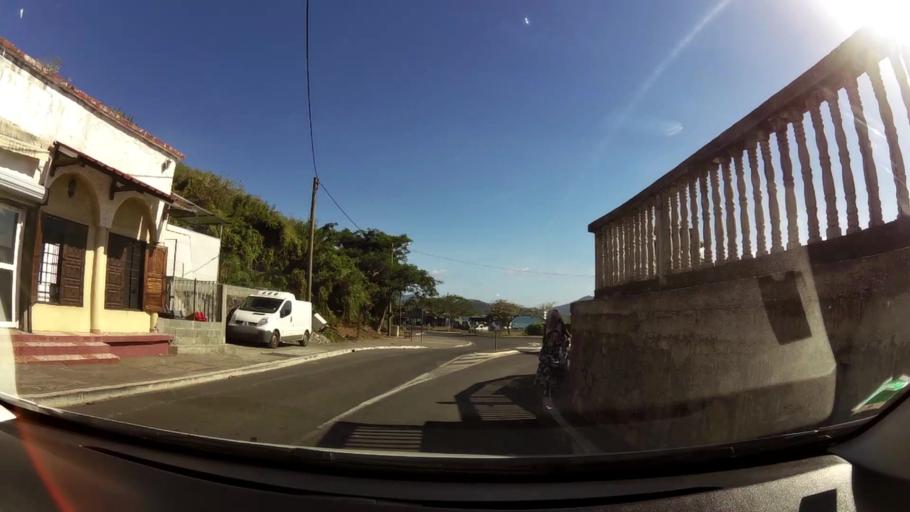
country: YT
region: Pamandzi
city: Pamandzi
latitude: -12.7897
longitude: 45.2686
